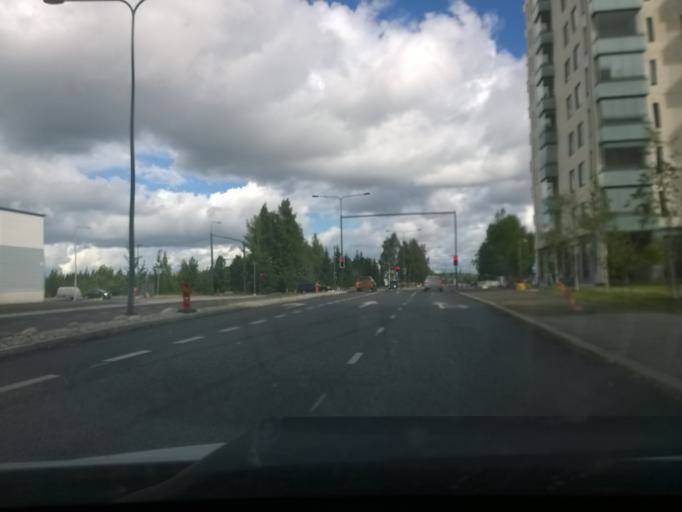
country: FI
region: Pirkanmaa
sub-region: Tampere
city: Tampere
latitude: 61.4729
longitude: 23.8716
